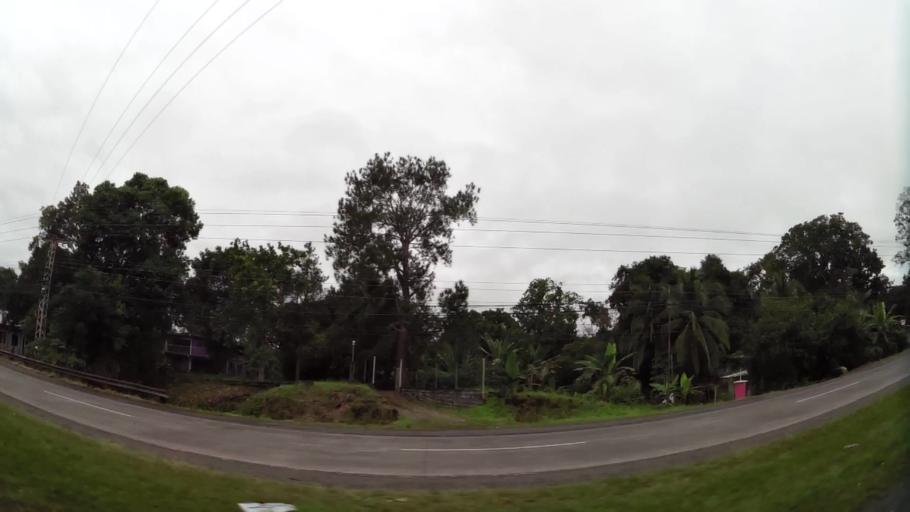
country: PA
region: Chiriqui
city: Boqueron
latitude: 8.4960
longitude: -82.5882
